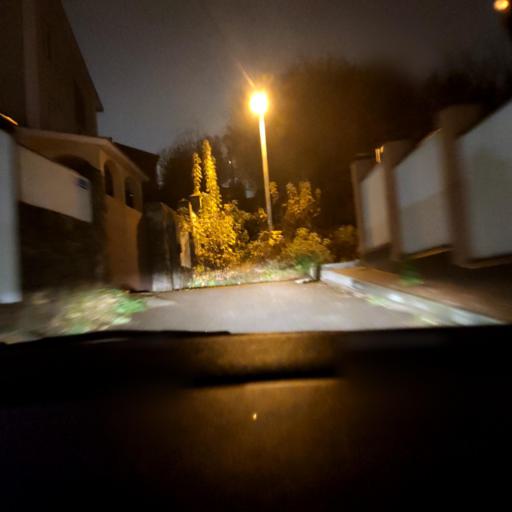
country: RU
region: Voronezj
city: Voronezh
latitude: 51.6984
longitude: 39.2101
